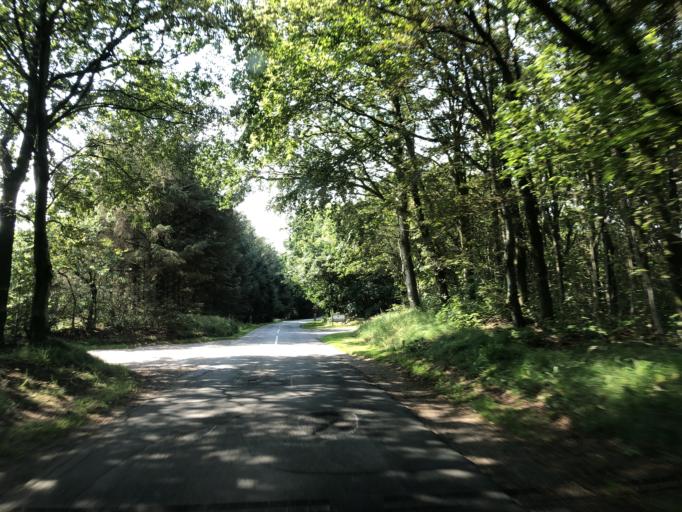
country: DK
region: Central Jutland
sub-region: Lemvig Kommune
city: Lemvig
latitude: 56.4392
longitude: 8.2860
